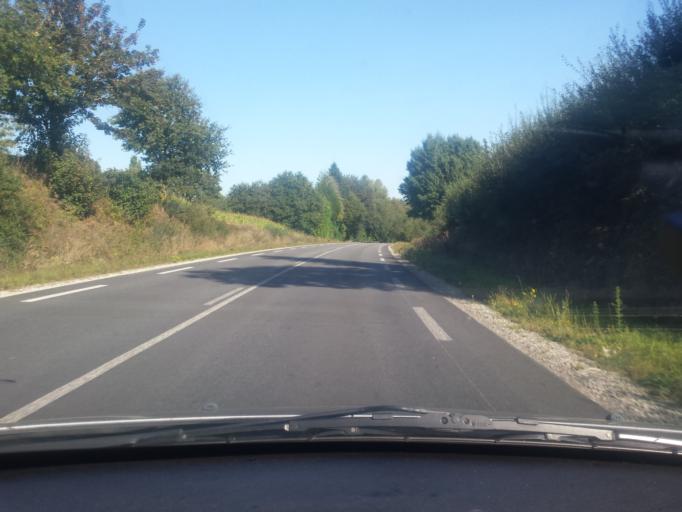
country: FR
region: Brittany
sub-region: Departement du Morbihan
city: Malguenac
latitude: 48.1001
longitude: -3.0660
